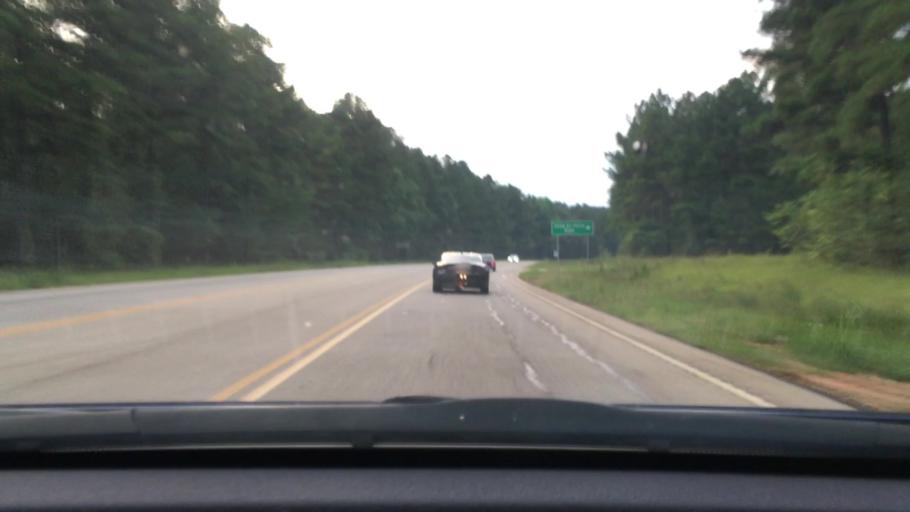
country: US
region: South Carolina
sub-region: Sumter County
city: Cherryvale
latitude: 33.9439
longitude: -80.4922
